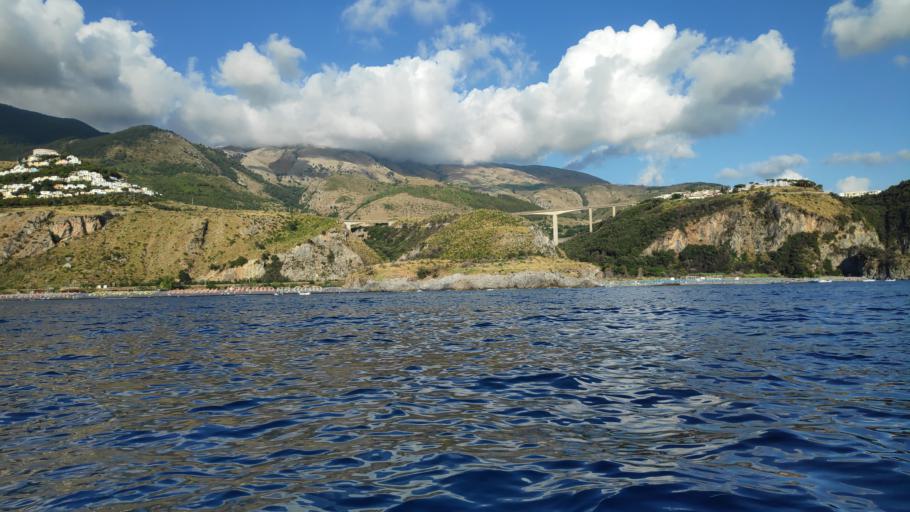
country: IT
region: Calabria
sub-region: Provincia di Cosenza
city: San Nicola Arcella
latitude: 39.8605
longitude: 15.7854
